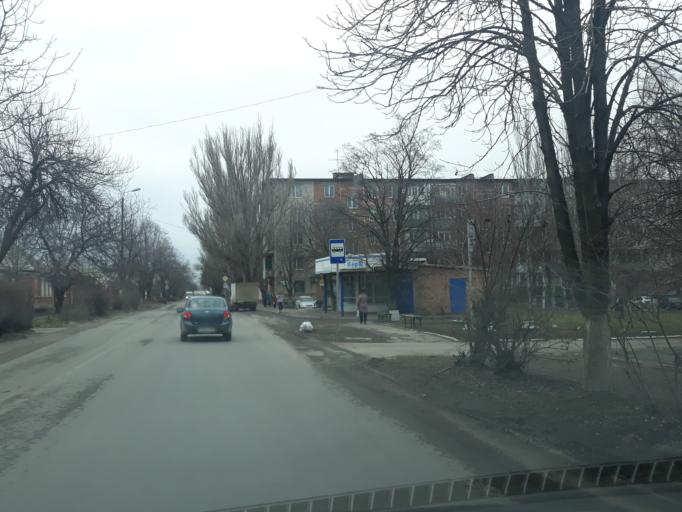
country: RU
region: Rostov
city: Taganrog
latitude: 47.2597
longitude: 38.9034
